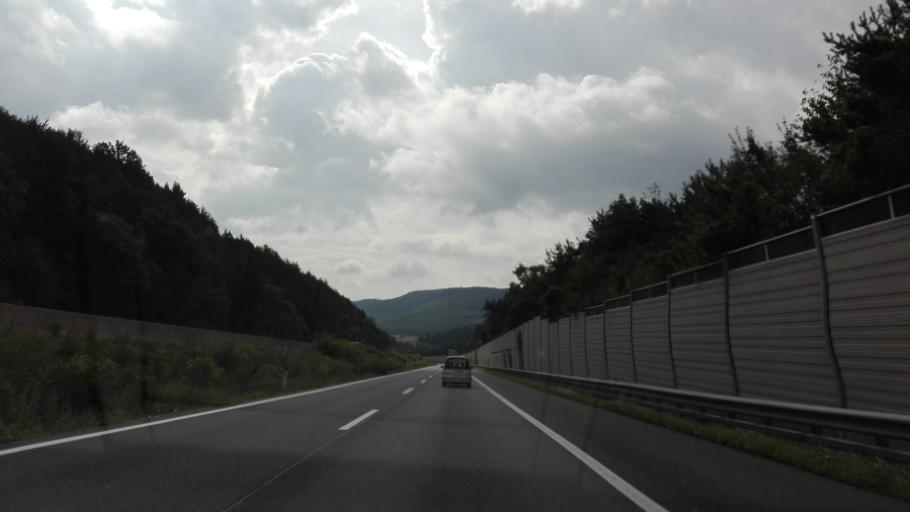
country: AT
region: Lower Austria
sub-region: Politischer Bezirk Baden
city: Klausen-Leopoldsdorf
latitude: 48.0941
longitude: 15.9943
